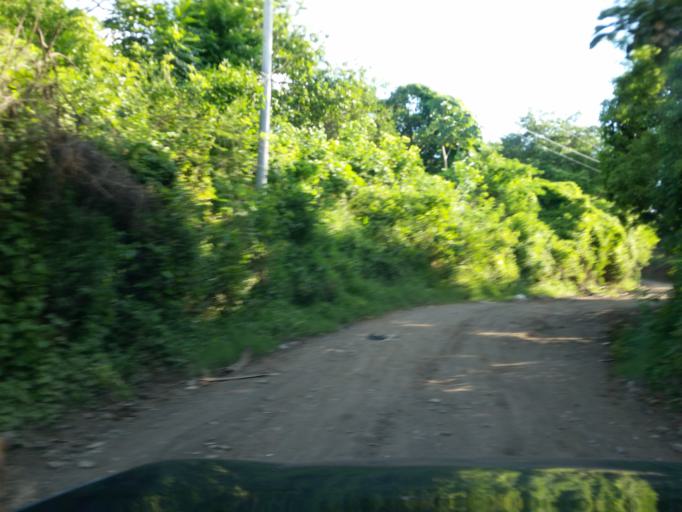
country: NI
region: Masaya
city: Ticuantepe
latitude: 12.0841
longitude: -86.2095
